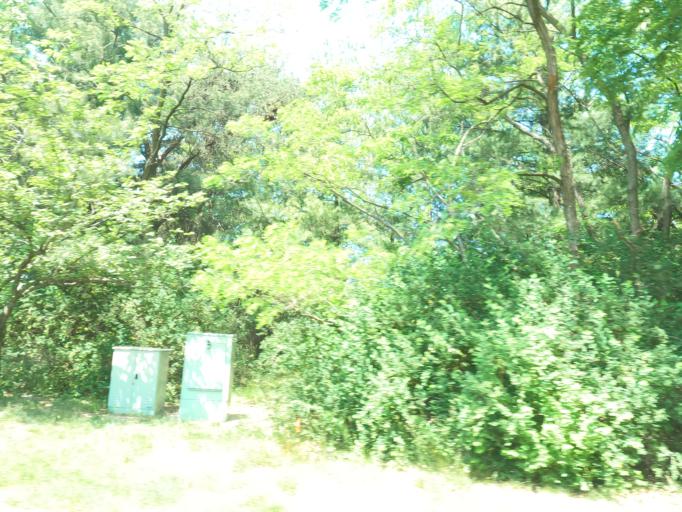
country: US
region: Maryland
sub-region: Howard County
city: Savage
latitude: 39.1752
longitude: -76.8096
